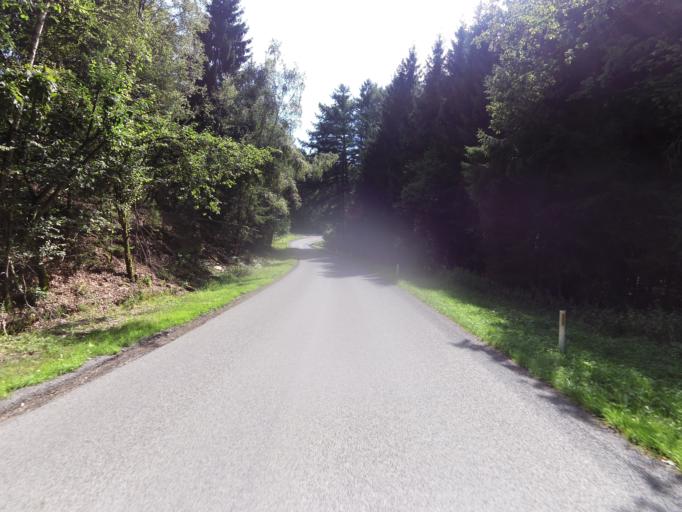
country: BE
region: Wallonia
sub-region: Province du Luxembourg
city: Saint-Hubert
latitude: 50.0418
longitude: 5.3554
